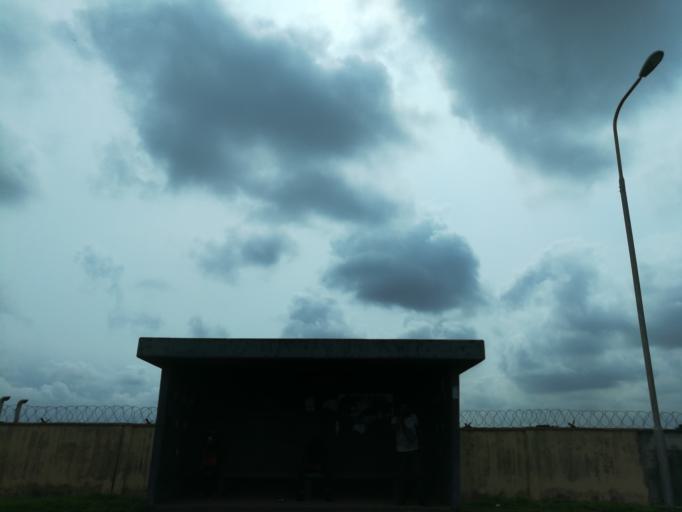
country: NG
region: Lagos
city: Oshodi
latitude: 6.5673
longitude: 3.3235
